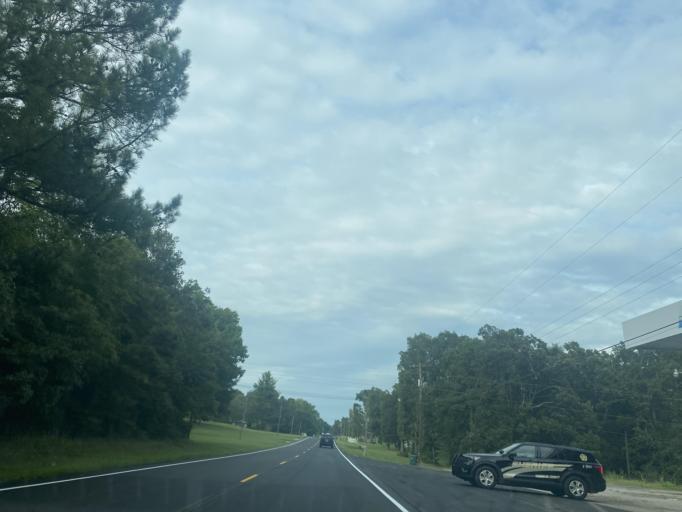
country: US
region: South Carolina
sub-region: Cherokee County
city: Blacksburg
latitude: 35.0934
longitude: -81.5563
